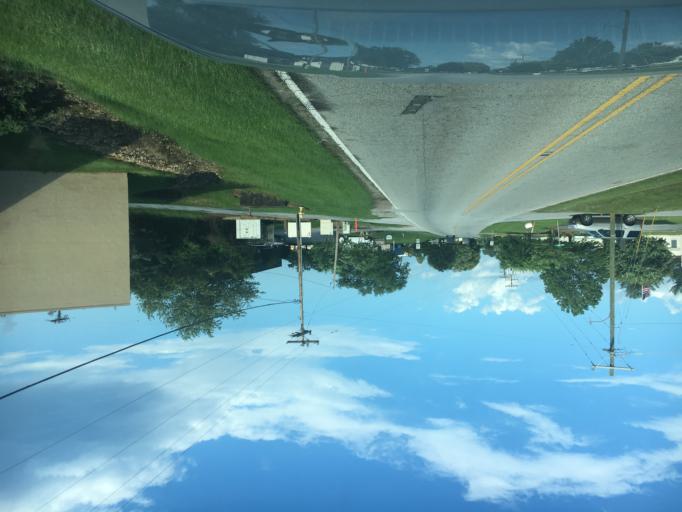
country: US
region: South Carolina
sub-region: Greenville County
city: Mauldin
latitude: 34.7946
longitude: -82.3063
